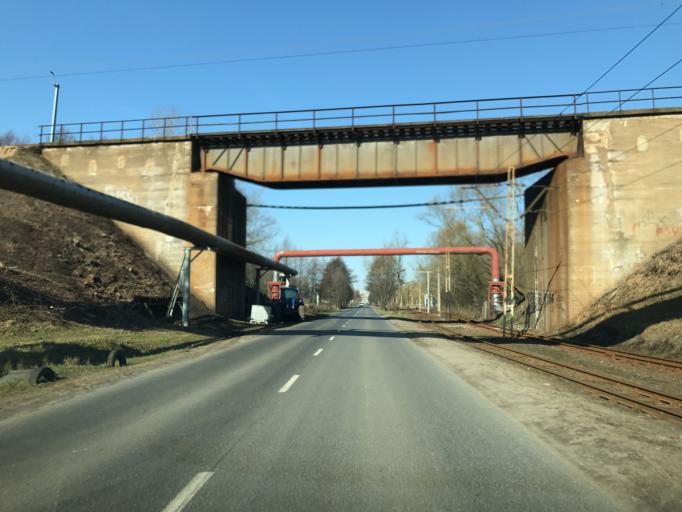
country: PL
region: Kujawsko-Pomorskie
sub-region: Powiat bydgoski
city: Osielsko
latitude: 53.1156
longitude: 18.1002
